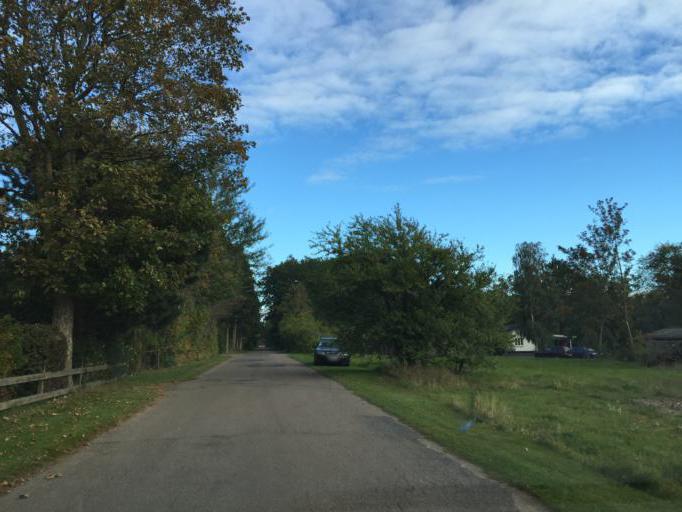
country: DK
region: Zealand
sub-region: Odsherred Kommune
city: Asnaes
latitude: 55.7975
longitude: 11.4959
